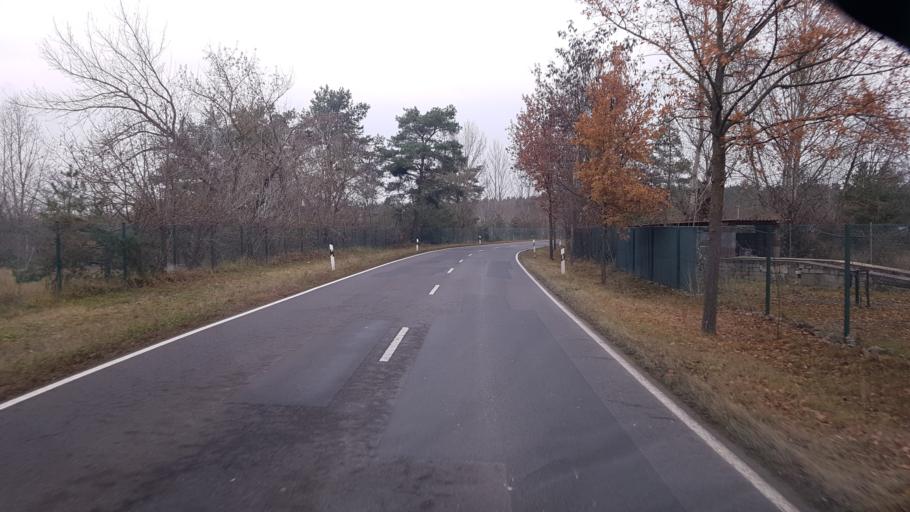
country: DE
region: Brandenburg
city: Eisenhuettenstadt
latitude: 52.1572
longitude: 14.6549
